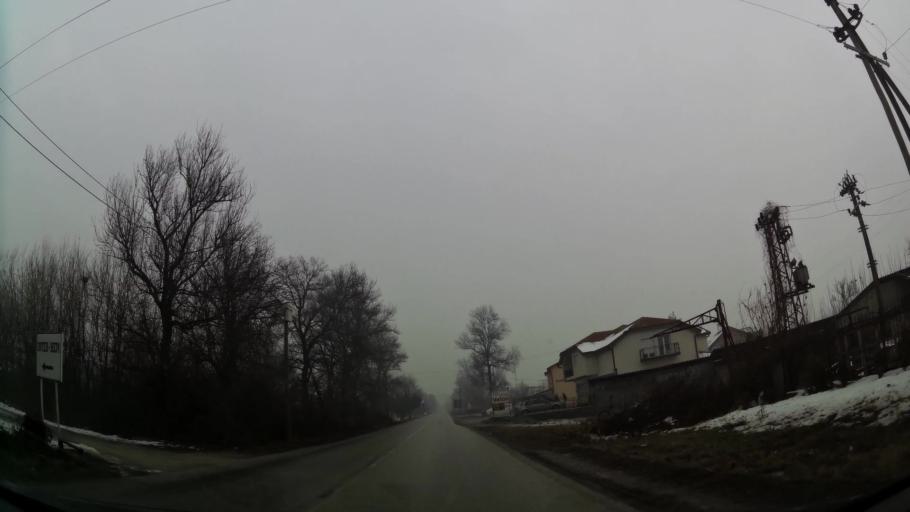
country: MK
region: Petrovec
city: Petrovec
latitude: 41.9424
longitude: 21.6068
